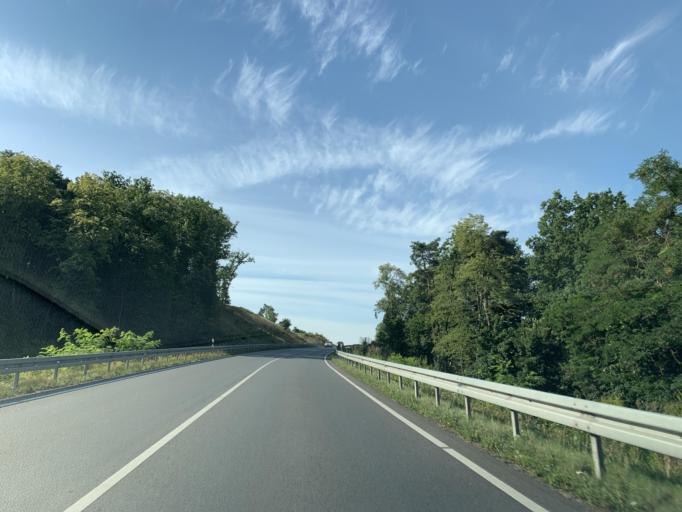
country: DE
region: Mecklenburg-Vorpommern
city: Neubrandenburg
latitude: 53.5436
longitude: 13.2739
